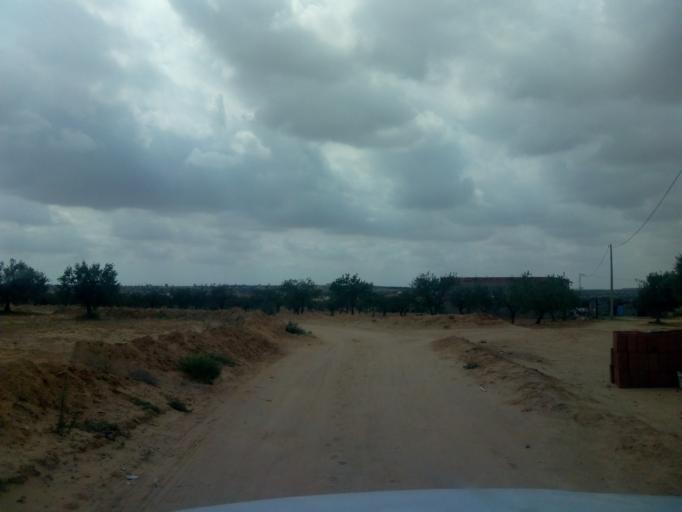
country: TN
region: Safaqis
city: Sfax
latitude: 34.7486
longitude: 10.4879
